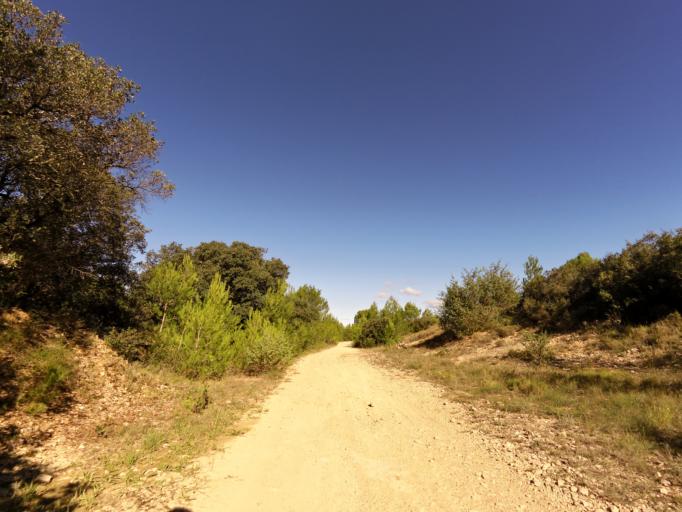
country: FR
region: Languedoc-Roussillon
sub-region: Departement de l'Herault
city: Villetelle
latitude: 43.7363
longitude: 4.1515
